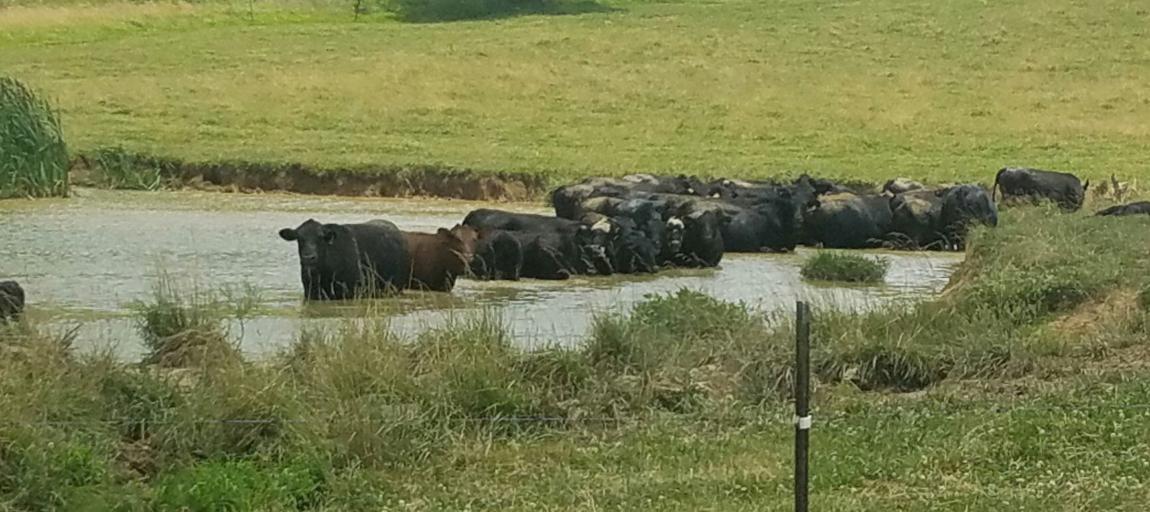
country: US
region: Kentucky
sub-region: Edmonson County
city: Brownsville
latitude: 37.3183
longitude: -86.0981
